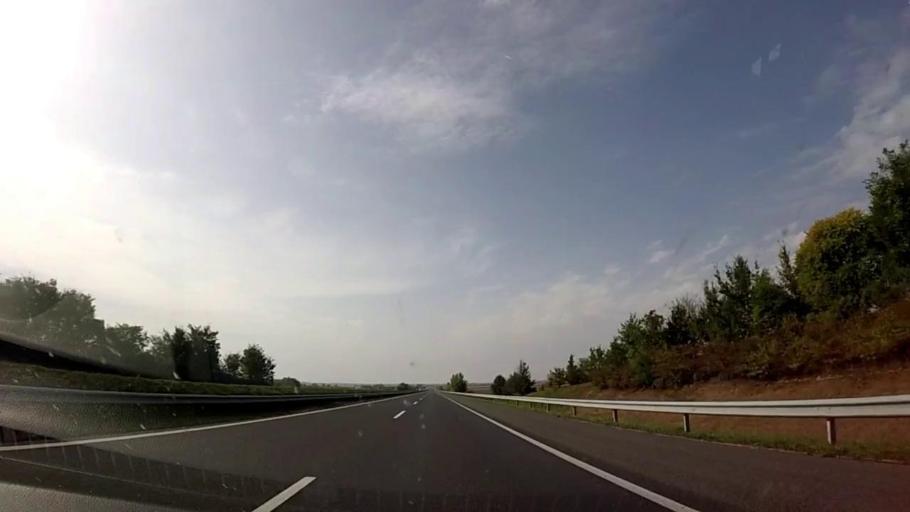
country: HU
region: Zala
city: Becsehely
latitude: 46.4336
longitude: 16.7949
